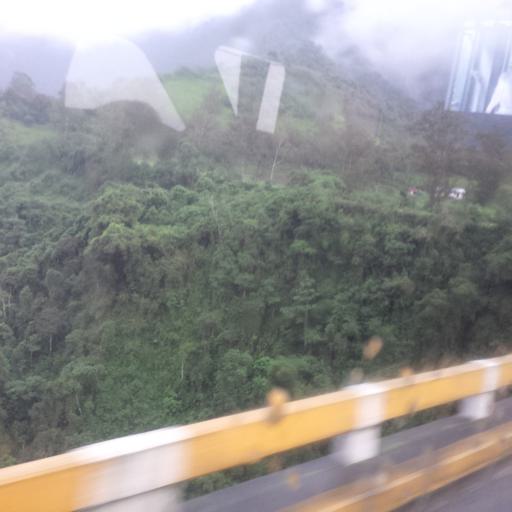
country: EC
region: Chimborazo
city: Alausi
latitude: -2.0559
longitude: -78.9850
